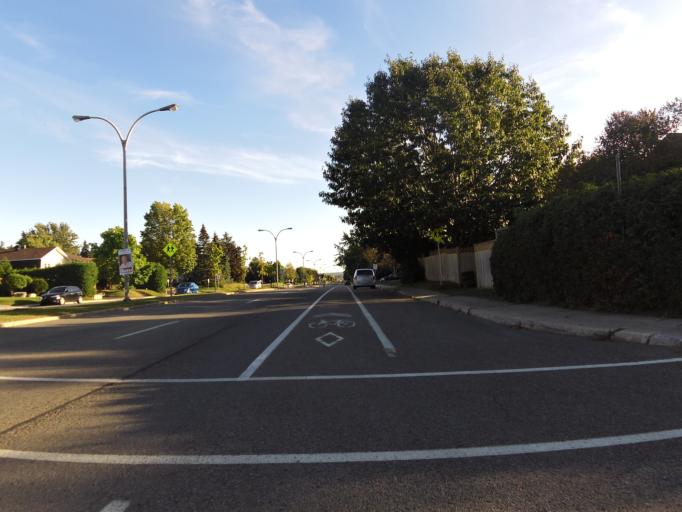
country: CA
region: Ontario
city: Bells Corners
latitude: 45.4064
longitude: -75.8385
